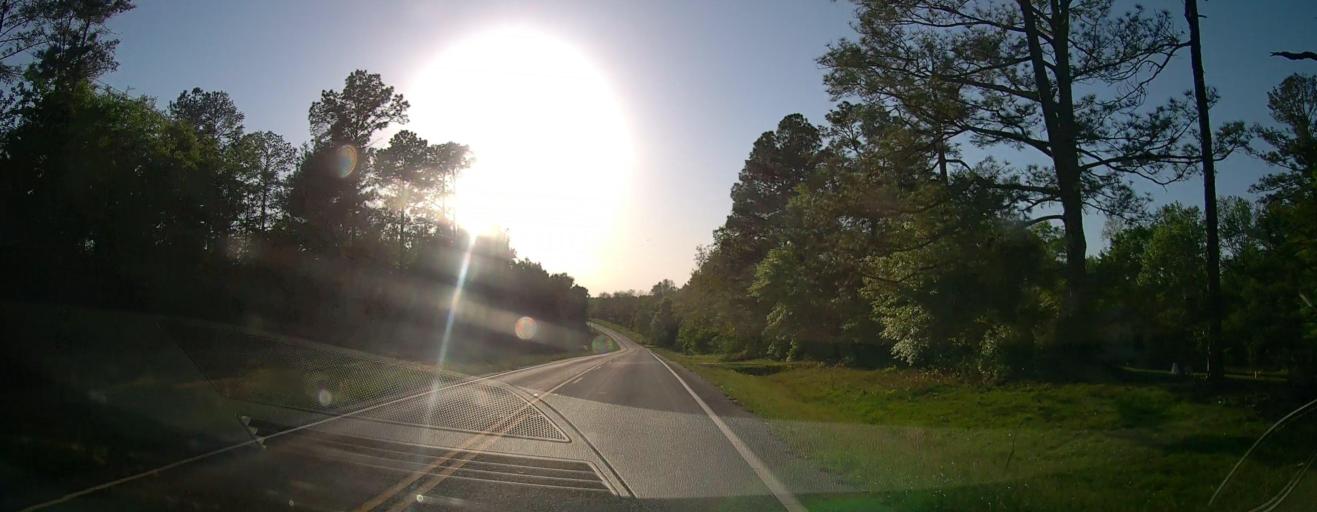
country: US
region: Georgia
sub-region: Macon County
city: Oglethorpe
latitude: 32.3191
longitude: -84.1901
